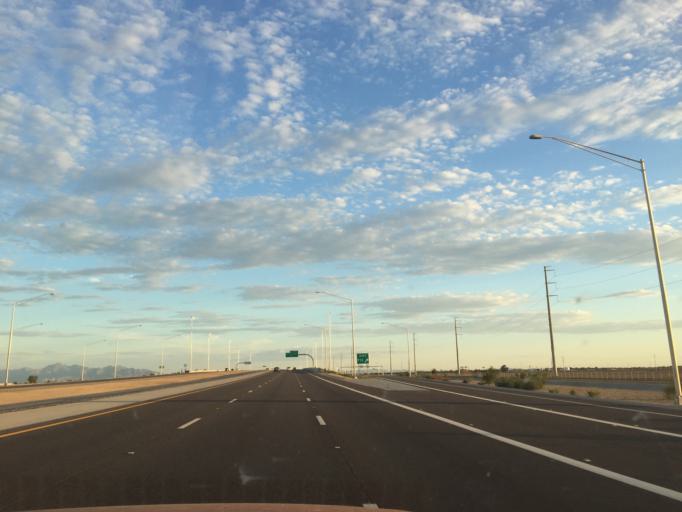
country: US
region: Arizona
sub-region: Maricopa County
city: Citrus Park
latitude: 33.5855
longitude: -112.4183
